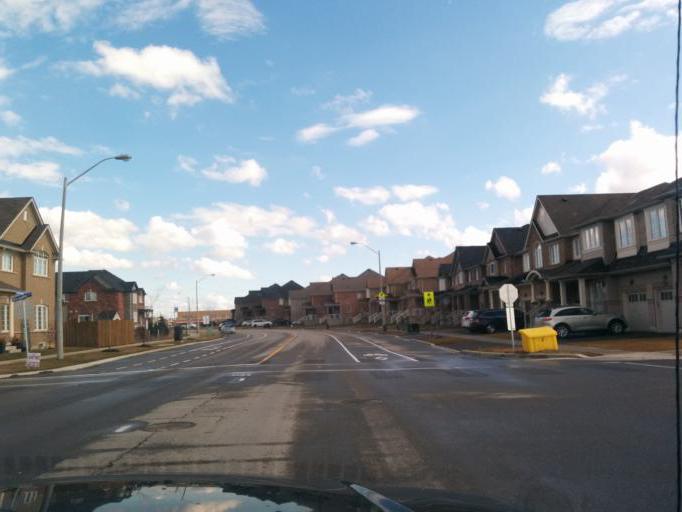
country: CA
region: Ontario
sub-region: Halton
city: Milton
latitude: 43.4978
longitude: -79.8651
